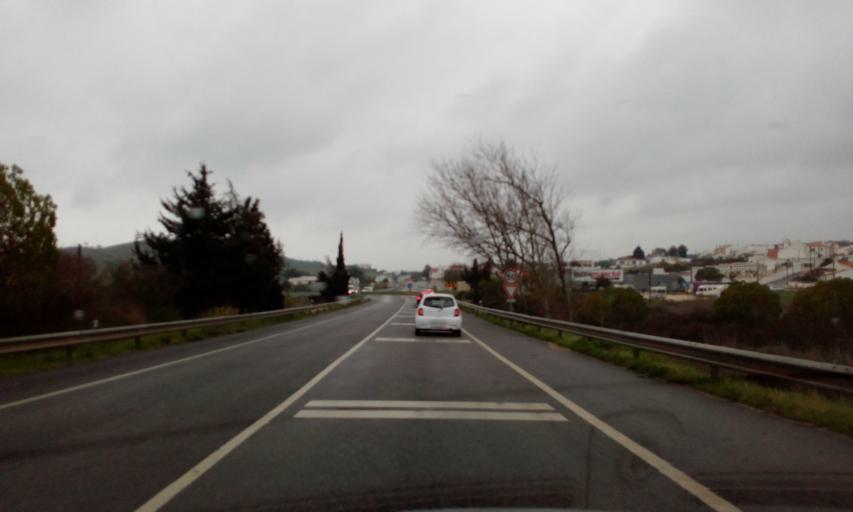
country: PT
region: Faro
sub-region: Vila do Bispo
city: Vila do Bispo
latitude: 37.0876
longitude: -8.8261
